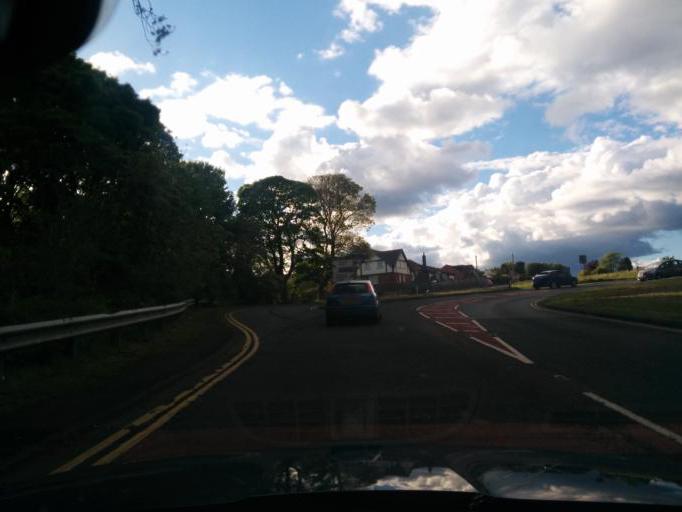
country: GB
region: England
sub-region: Northumberland
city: Bedlington
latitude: 55.1141
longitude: -1.6229
